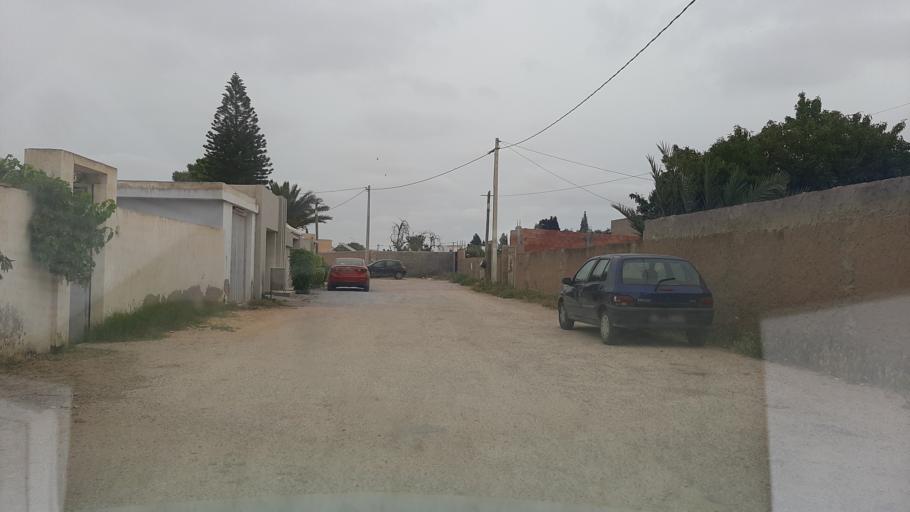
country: TN
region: Safaqis
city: Al Qarmadah
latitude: 34.7909
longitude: 10.7604
